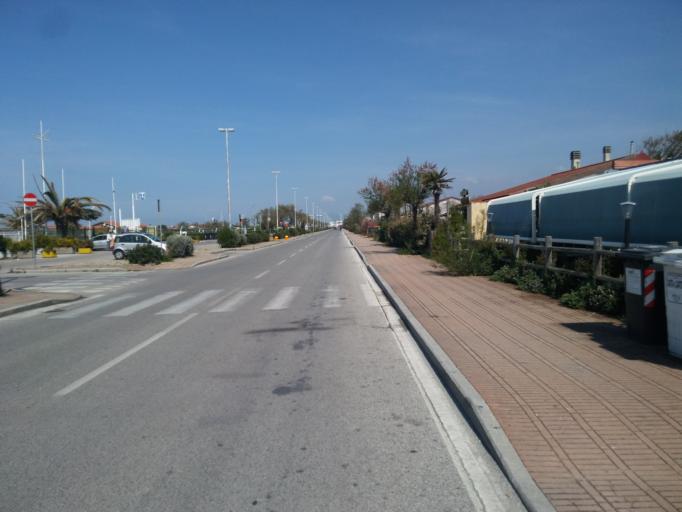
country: IT
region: Tuscany
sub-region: Provincia di Lucca
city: Viareggio
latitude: 43.8481
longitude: 10.2471
